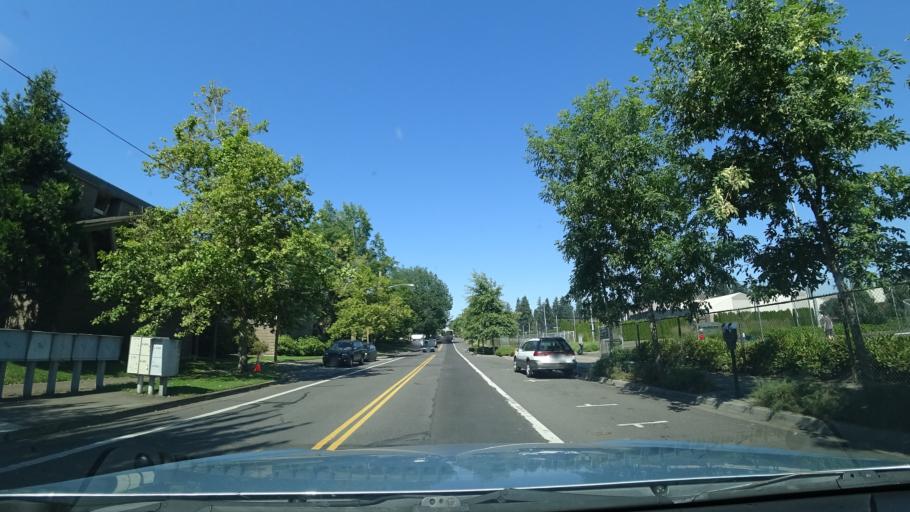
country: US
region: Oregon
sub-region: Lane County
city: Eugene
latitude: 44.0400
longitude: -123.0708
